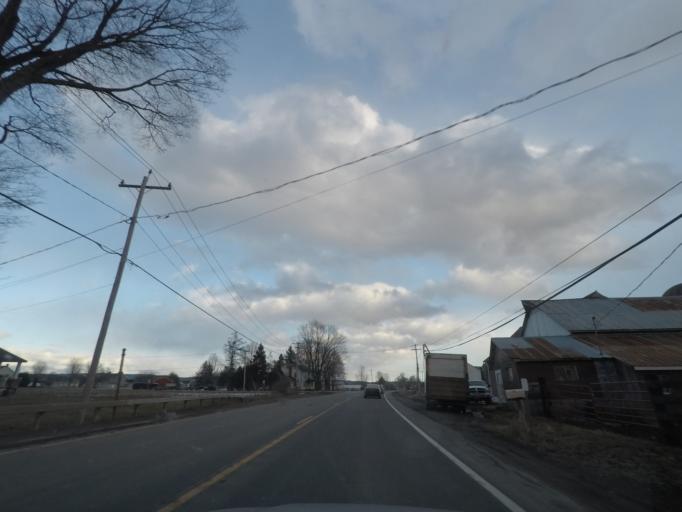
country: US
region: New York
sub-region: Herkimer County
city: Frankfort
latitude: 43.0923
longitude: -75.1348
